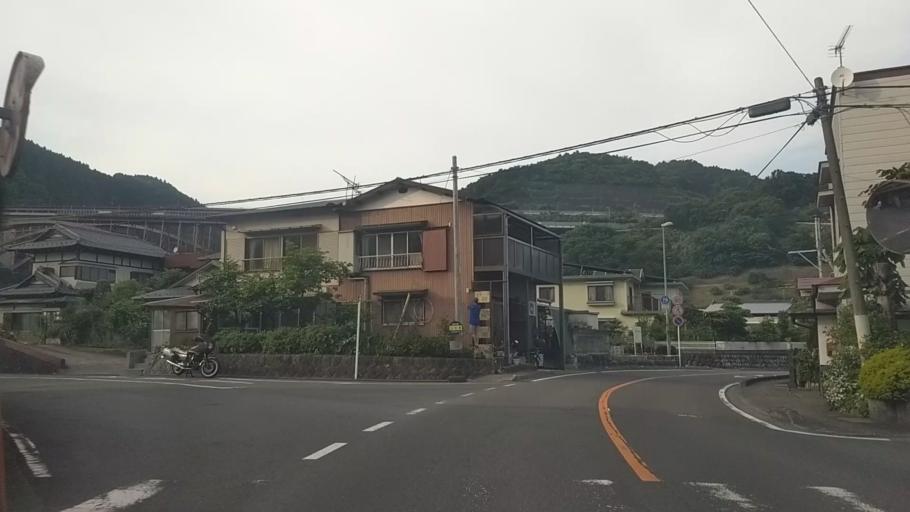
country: JP
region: Kanagawa
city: Odawara
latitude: 35.3594
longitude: 139.0717
